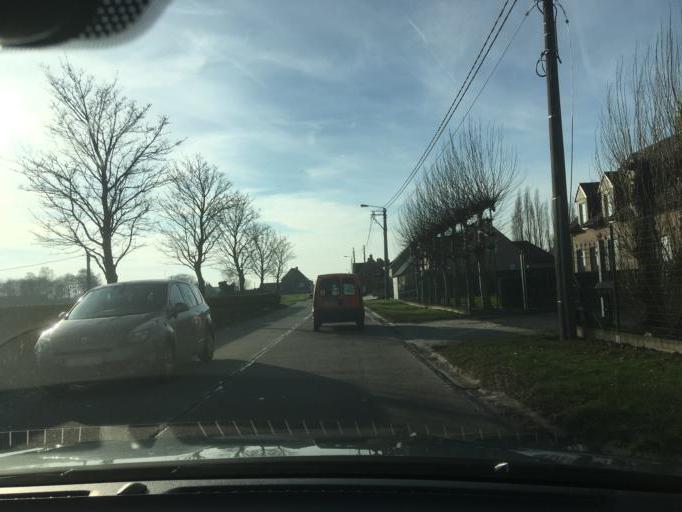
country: BE
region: Flanders
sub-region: Provincie West-Vlaanderen
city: Wielsbeke
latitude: 50.9247
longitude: 3.3848
